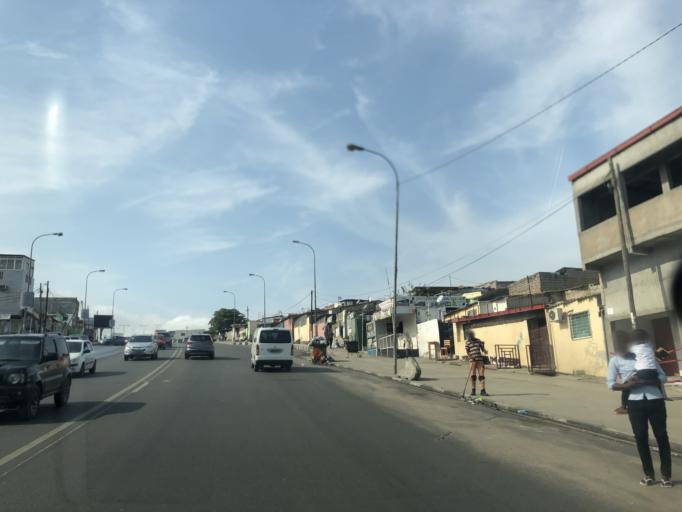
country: AO
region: Luanda
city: Luanda
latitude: -8.8309
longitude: 13.2256
